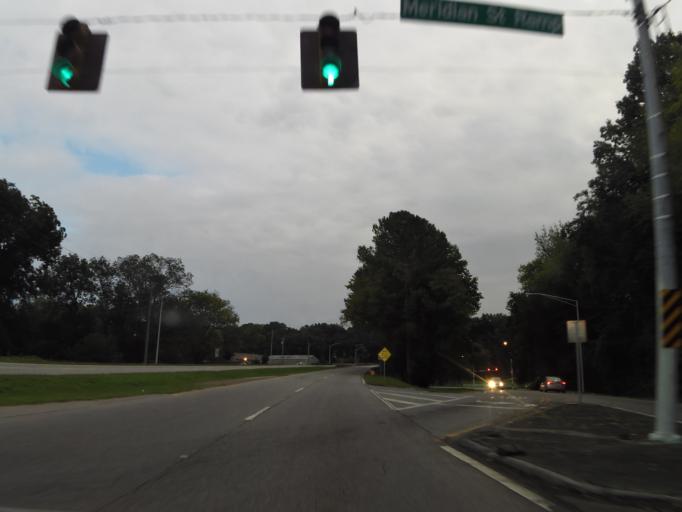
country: US
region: Alabama
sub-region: Madison County
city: Huntsville
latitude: 34.7616
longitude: -86.5772
